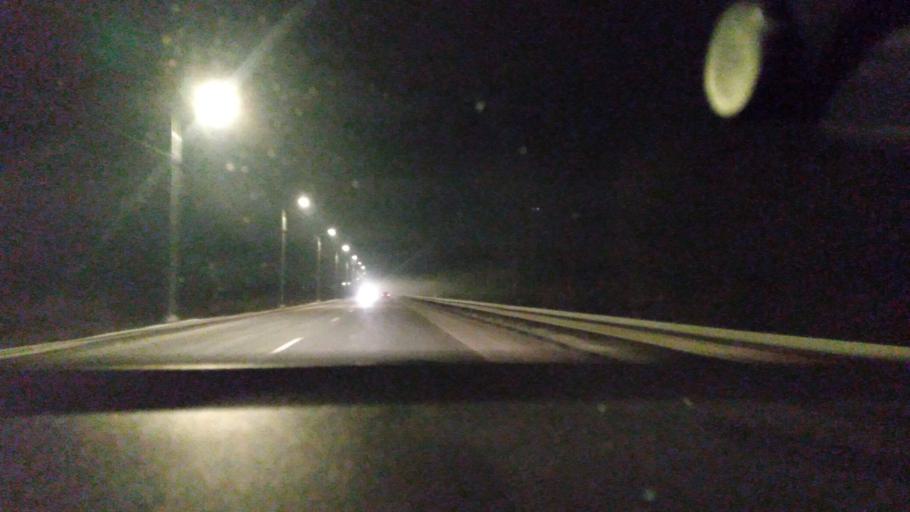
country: RU
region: Moskovskaya
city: Yegor'yevsk
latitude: 55.4415
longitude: 39.0183
